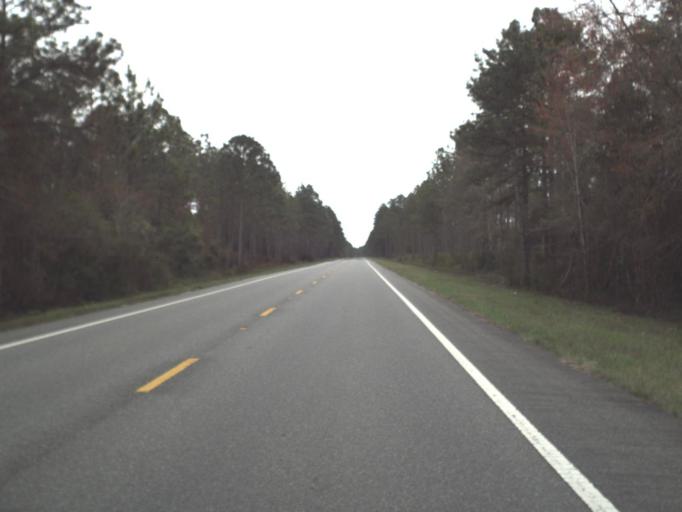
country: US
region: Florida
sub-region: Gadsden County
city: Midway
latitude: 30.3689
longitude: -84.5462
